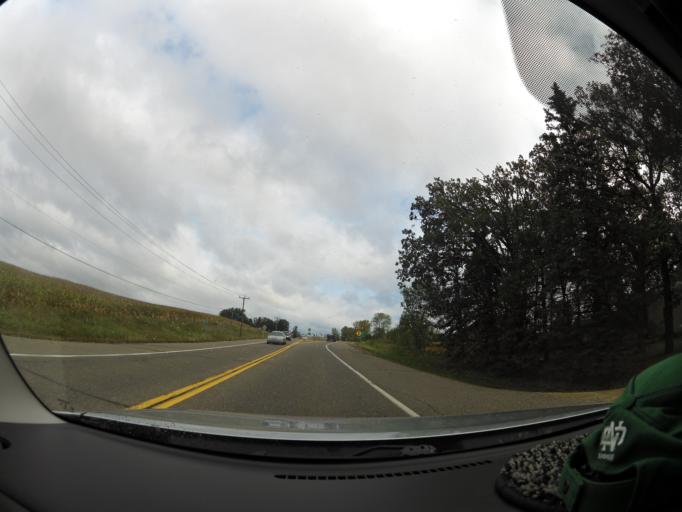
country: US
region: Minnesota
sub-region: Washington County
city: Lake Elmo
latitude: 44.9421
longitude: -92.8627
